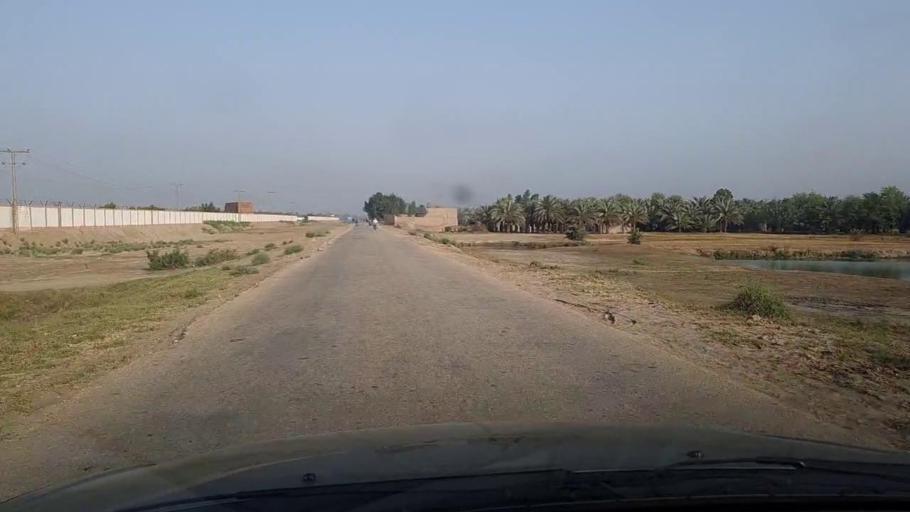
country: PK
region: Sindh
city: Khairpur
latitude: 27.5472
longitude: 68.6983
